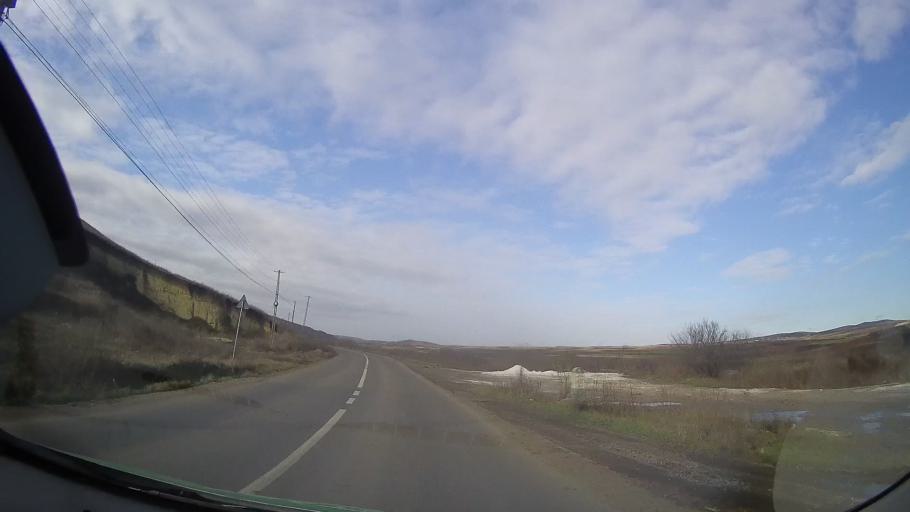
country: RO
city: Barza
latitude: 46.5486
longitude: 24.1218
